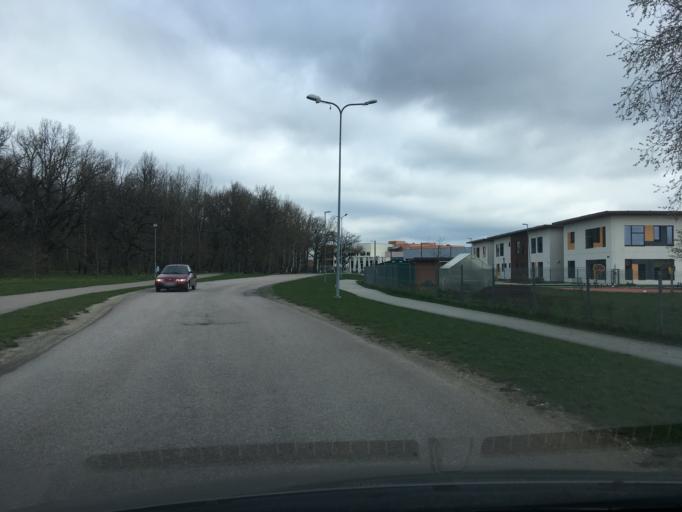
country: EE
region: Harju
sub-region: Rae vald
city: Jueri
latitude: 59.3540
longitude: 24.9044
